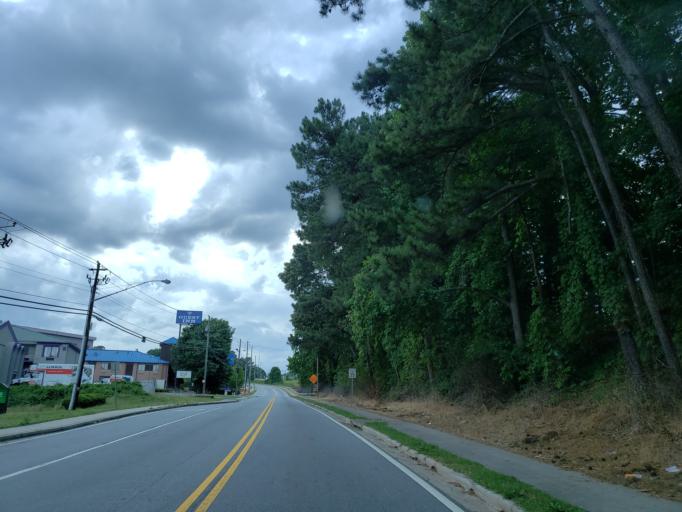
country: US
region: Georgia
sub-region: Cobb County
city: Mableton
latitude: 33.7724
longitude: -84.5546
